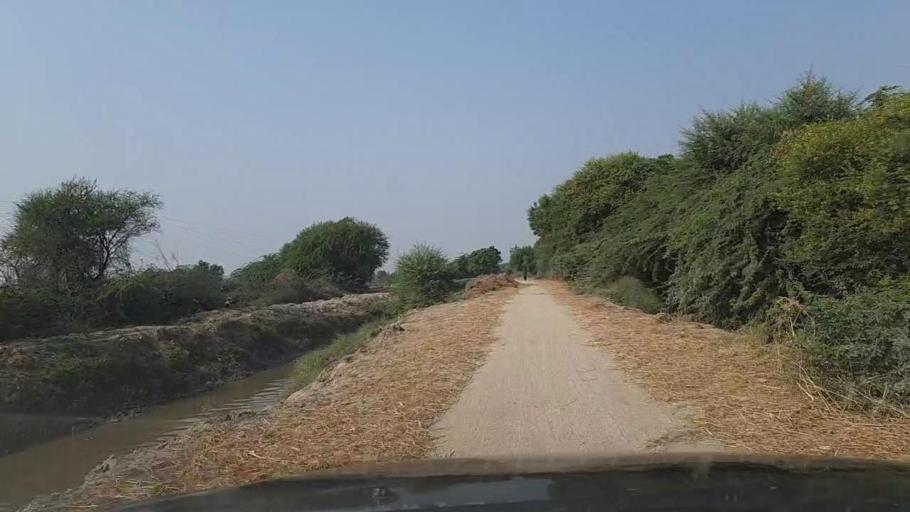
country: PK
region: Sindh
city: Mirpur Batoro
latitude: 24.7037
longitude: 68.2552
